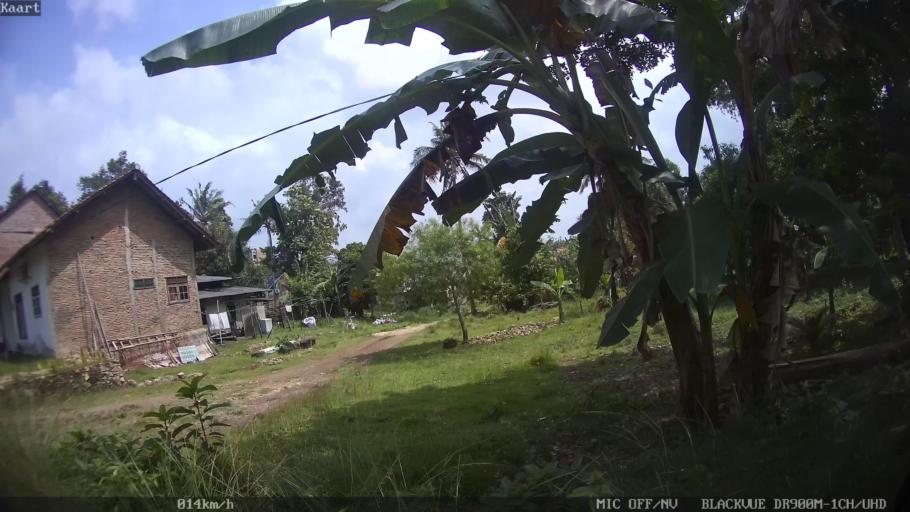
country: ID
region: Lampung
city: Kedaton
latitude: -5.3315
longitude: 105.2948
